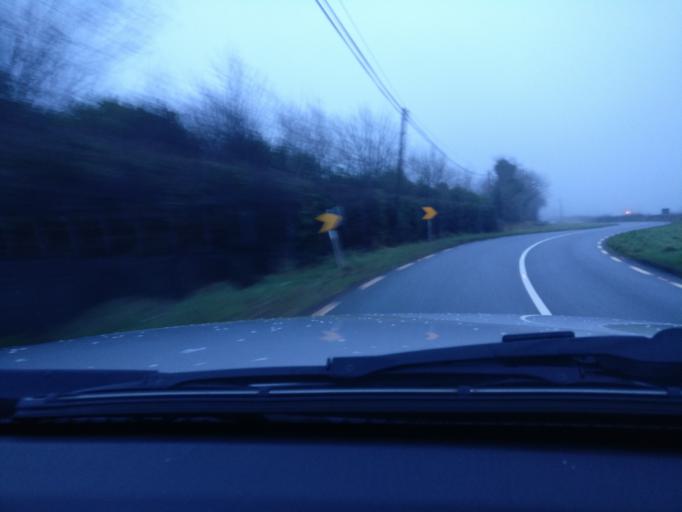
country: IE
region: Leinster
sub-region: An Mhi
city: Athboy
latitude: 53.6097
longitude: -6.9606
